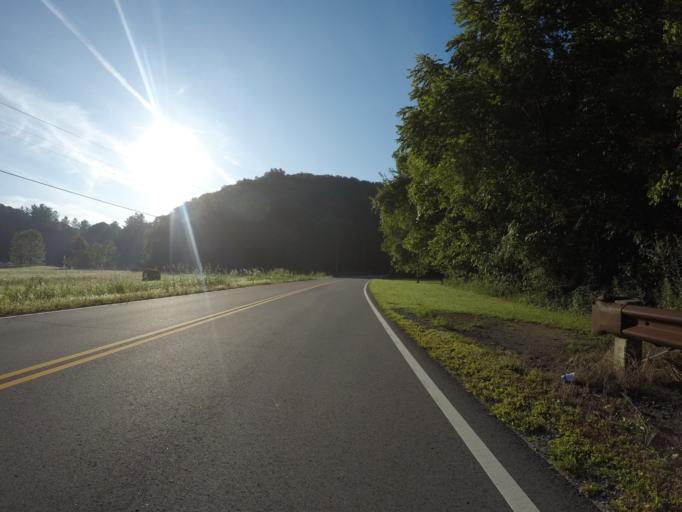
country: US
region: Ohio
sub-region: Lawrence County
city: Ironton
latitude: 38.6137
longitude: -82.5930
